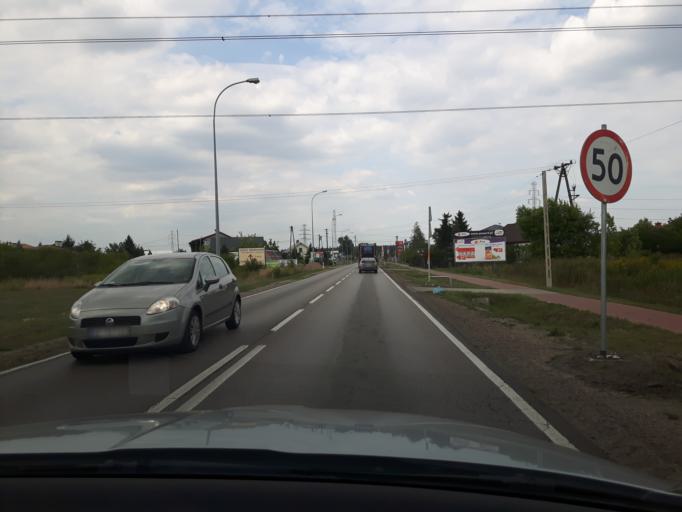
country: PL
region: Masovian Voivodeship
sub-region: Powiat legionowski
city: Stanislawow Pierwszy
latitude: 52.3714
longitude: 21.0289
